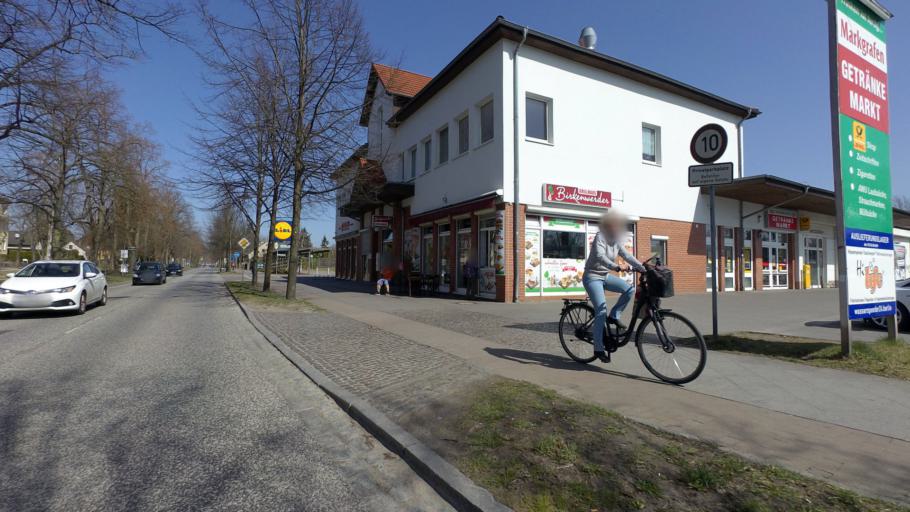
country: DE
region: Brandenburg
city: Birkenwerder
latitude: 52.6934
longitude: 13.2765
